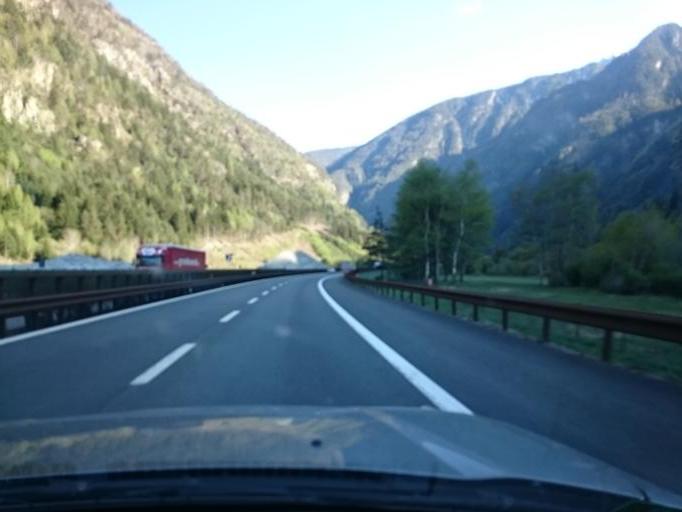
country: IT
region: Trentino-Alto Adige
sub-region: Bolzano
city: Campo di Trens
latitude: 46.8290
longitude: 11.5357
